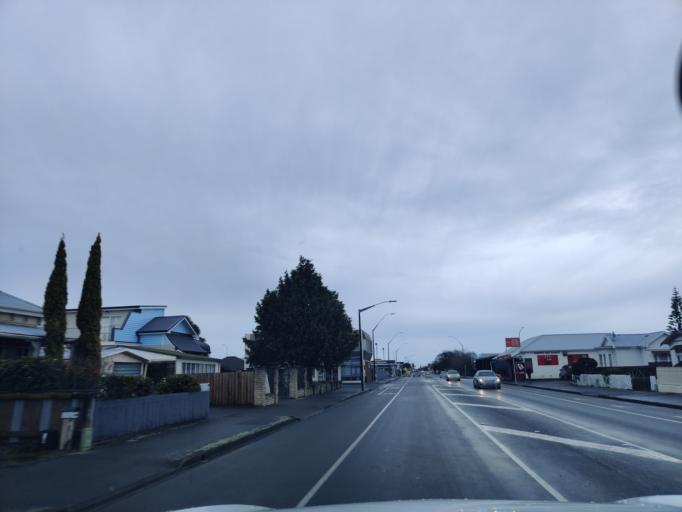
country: NZ
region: Manawatu-Wanganui
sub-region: Palmerston North City
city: Palmerston North
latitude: -40.3475
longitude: 175.6116
